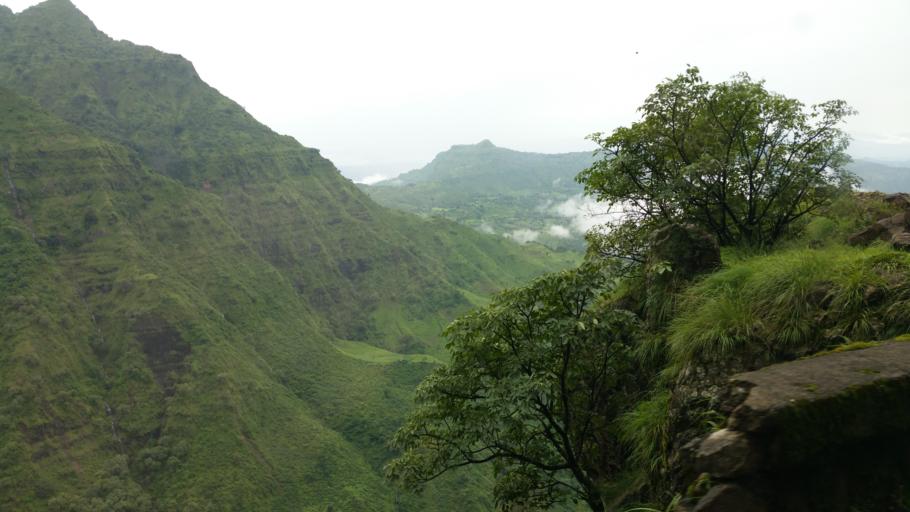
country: ET
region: Amhara
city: Debark'
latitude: 13.1998
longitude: 37.8864
